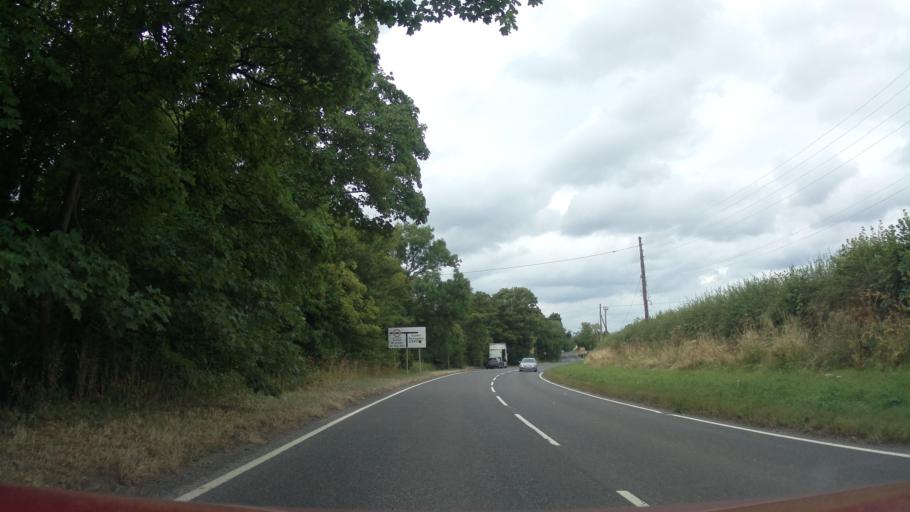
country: GB
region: England
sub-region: Derbyshire
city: Melbourne
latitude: 52.8093
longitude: -1.3781
